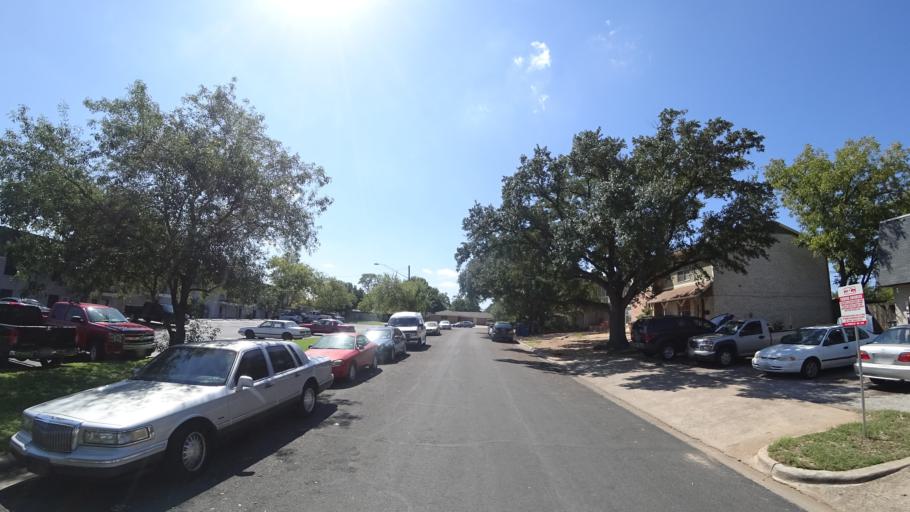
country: US
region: Texas
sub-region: Travis County
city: Austin
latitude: 30.3114
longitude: -97.6893
